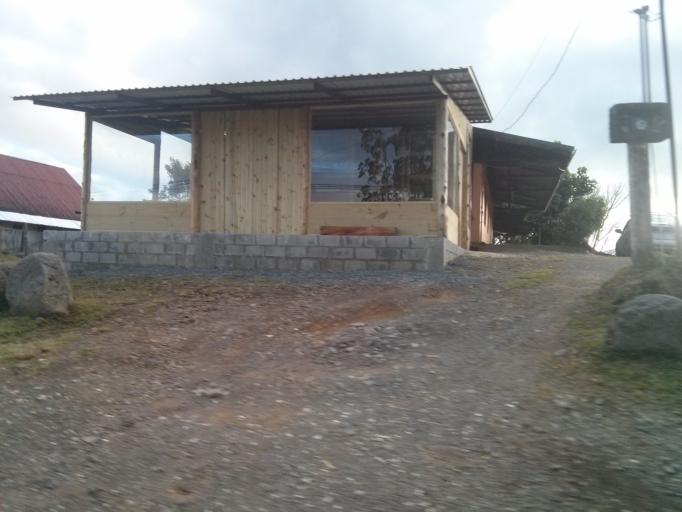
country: CR
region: Cartago
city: Turrialba
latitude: 9.9581
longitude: -83.7173
